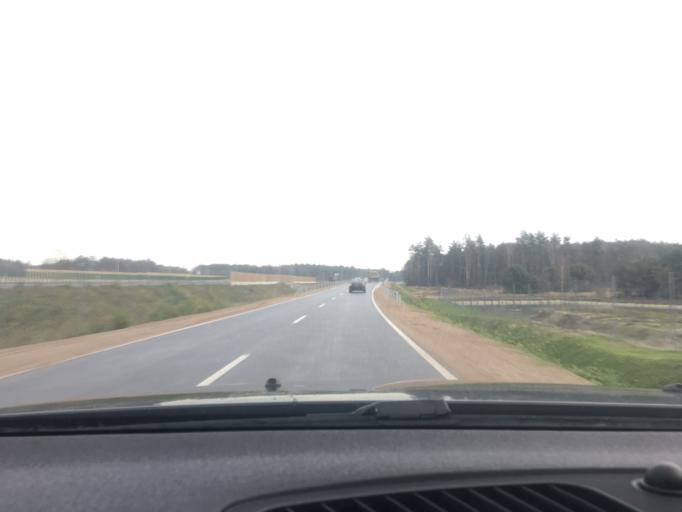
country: PL
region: Swietokrzyskie
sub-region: Powiat jedrzejowski
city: Jedrzejow
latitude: 50.6836
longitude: 20.3563
